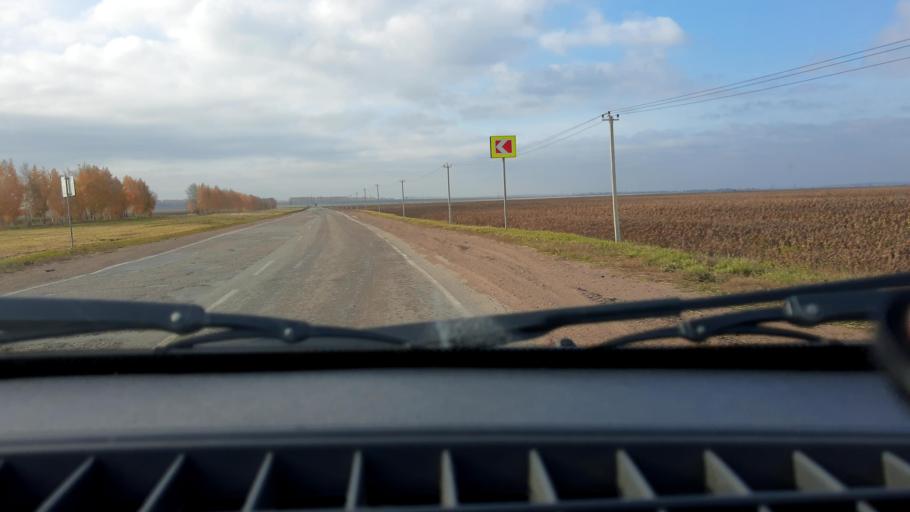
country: RU
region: Bashkortostan
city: Kabakovo
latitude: 54.5470
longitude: 56.0849
